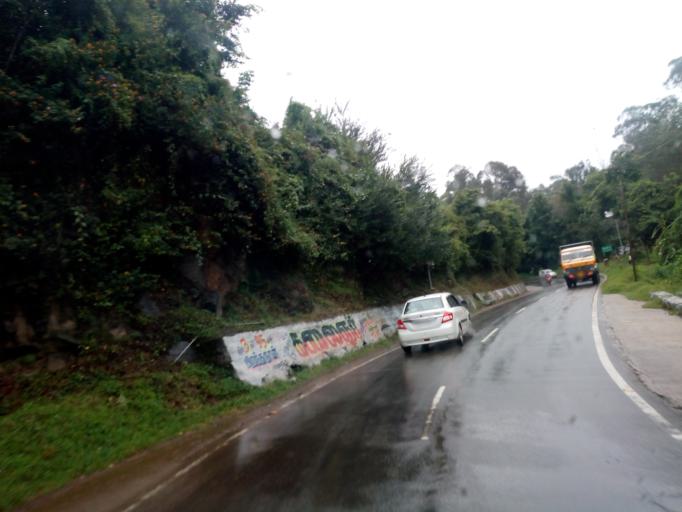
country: IN
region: Tamil Nadu
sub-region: Nilgiri
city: Wellington
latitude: 11.3531
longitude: 76.7851
